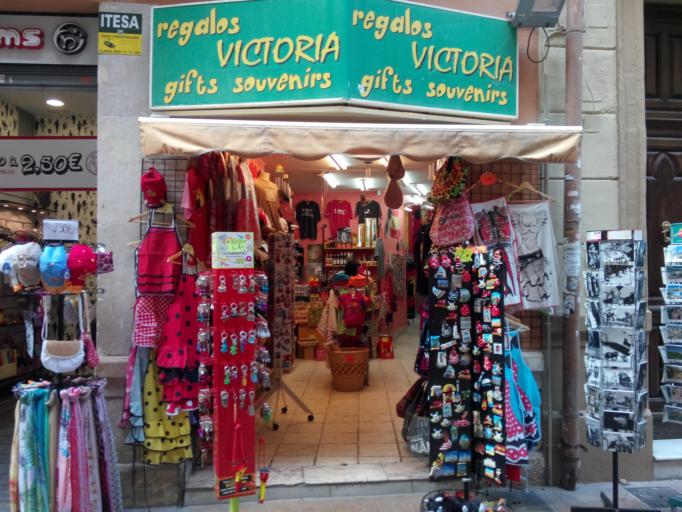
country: ES
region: Andalusia
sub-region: Provincia de Malaga
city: Malaga
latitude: 36.7222
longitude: -4.4188
